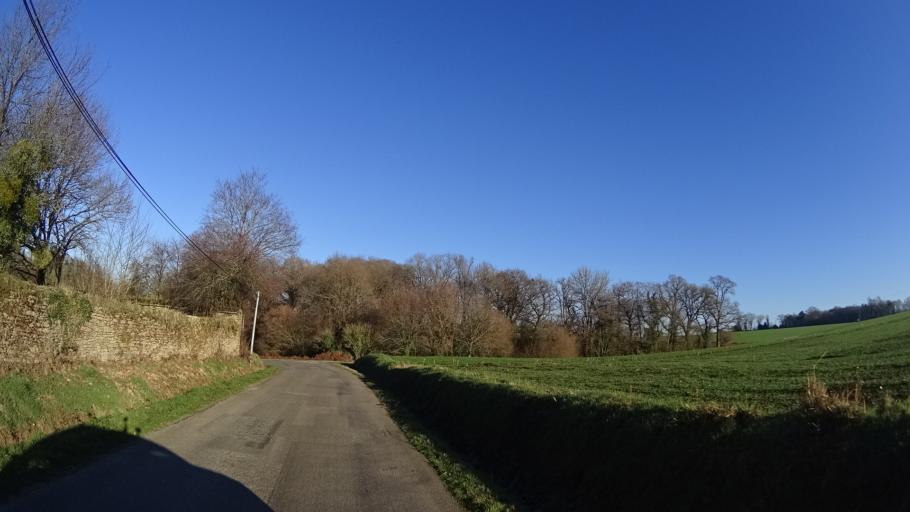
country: FR
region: Brittany
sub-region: Departement du Morbihan
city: Saint-Jacut-les-Pins
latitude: 47.6713
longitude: -2.2047
